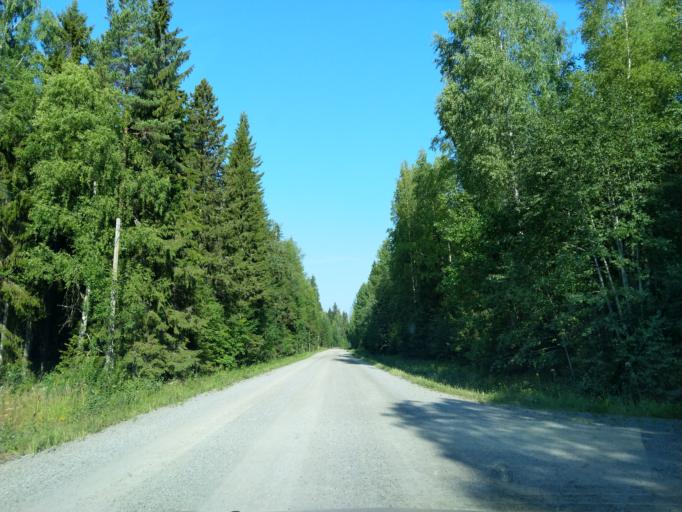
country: FI
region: Satakunta
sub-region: Pori
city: Laengelmaeki
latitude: 61.7316
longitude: 22.1765
